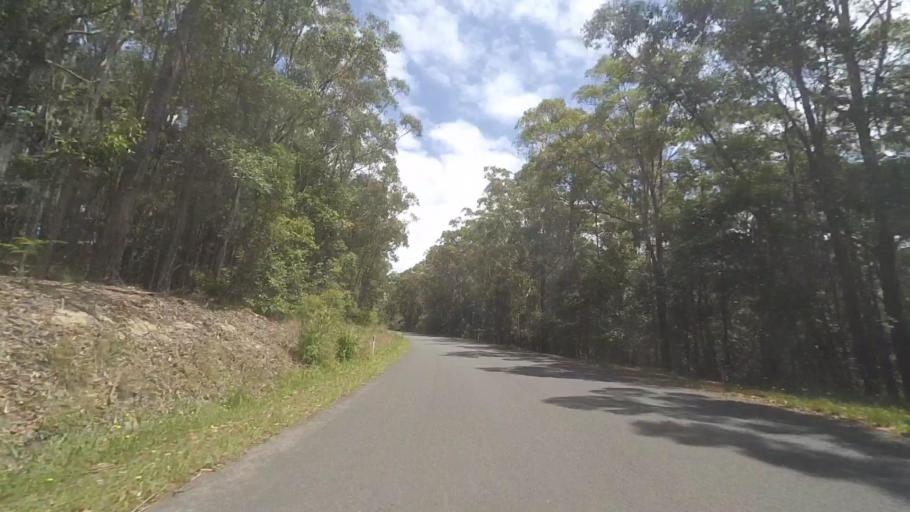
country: AU
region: New South Wales
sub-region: Shoalhaven Shire
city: Milton
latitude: -35.3992
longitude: 150.3663
